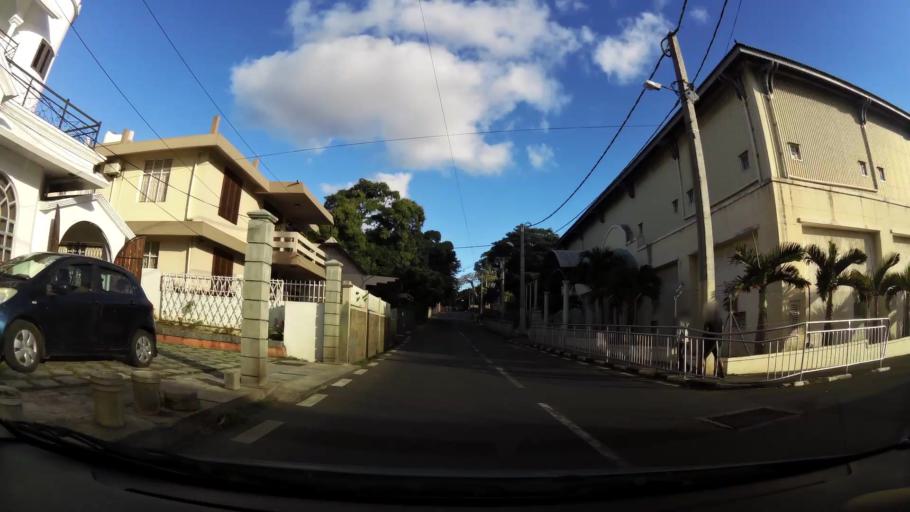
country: MU
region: Moka
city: Moka
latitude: -20.2254
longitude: 57.4636
